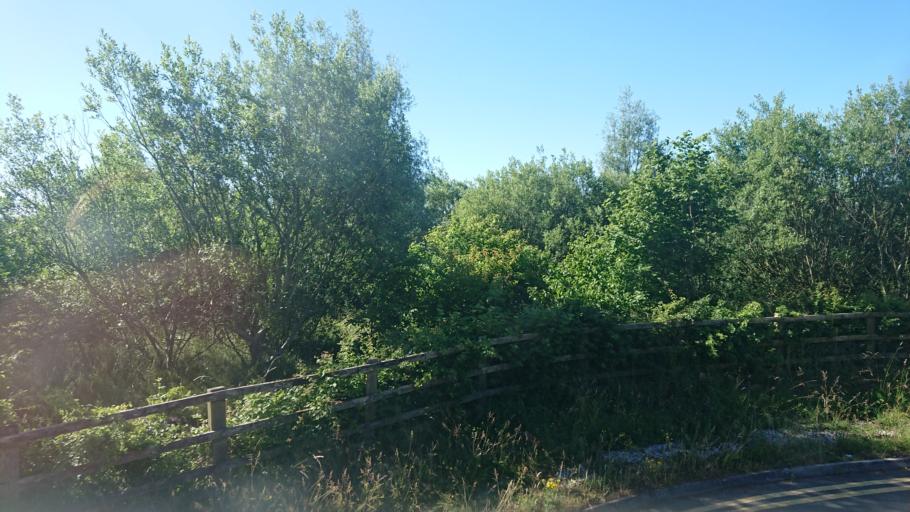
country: GB
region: England
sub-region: Lancashire
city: Galgate
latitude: 54.0020
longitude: -2.7887
